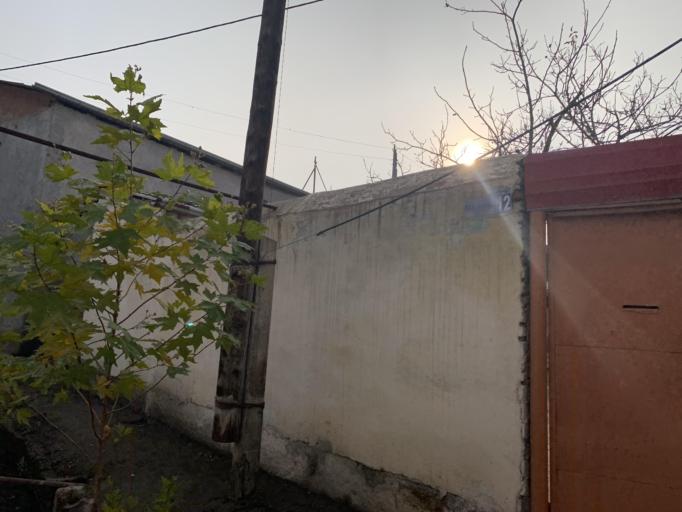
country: UZ
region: Fergana
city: Qo`qon
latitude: 40.5411
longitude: 70.9278
